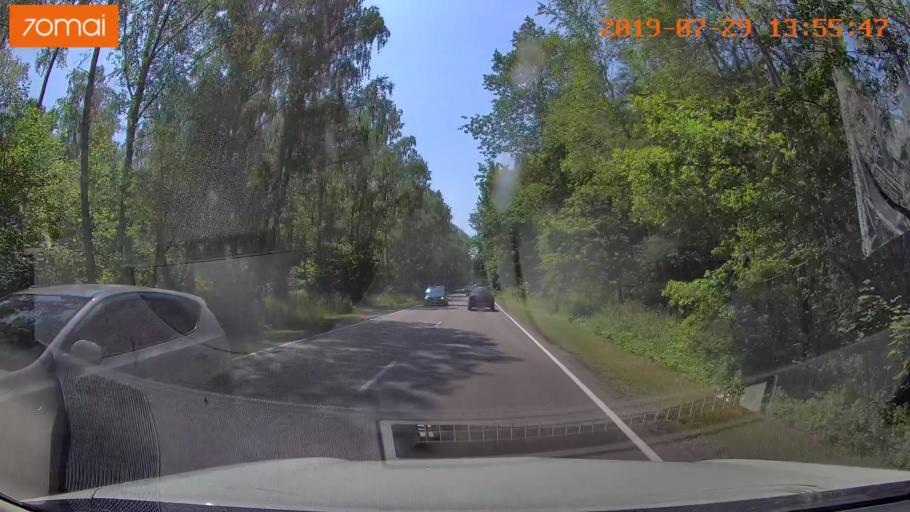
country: RU
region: Kaliningrad
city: Primorsk
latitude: 54.7125
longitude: 19.9538
